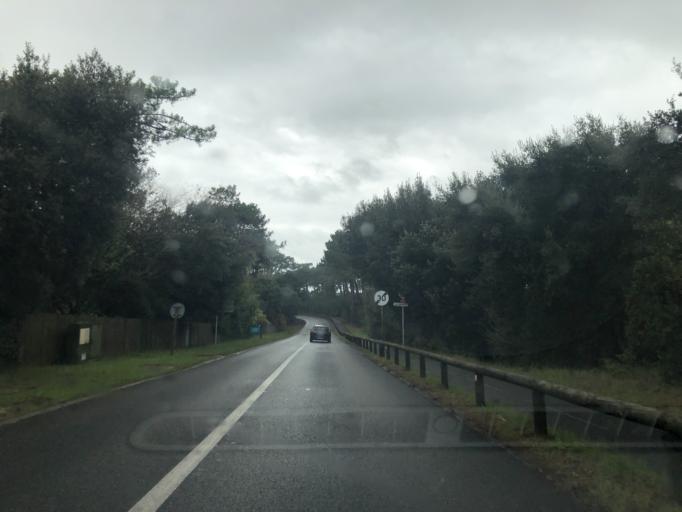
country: FR
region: Aquitaine
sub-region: Departement de la Gironde
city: Arcachon
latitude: 44.6935
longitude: -1.2365
